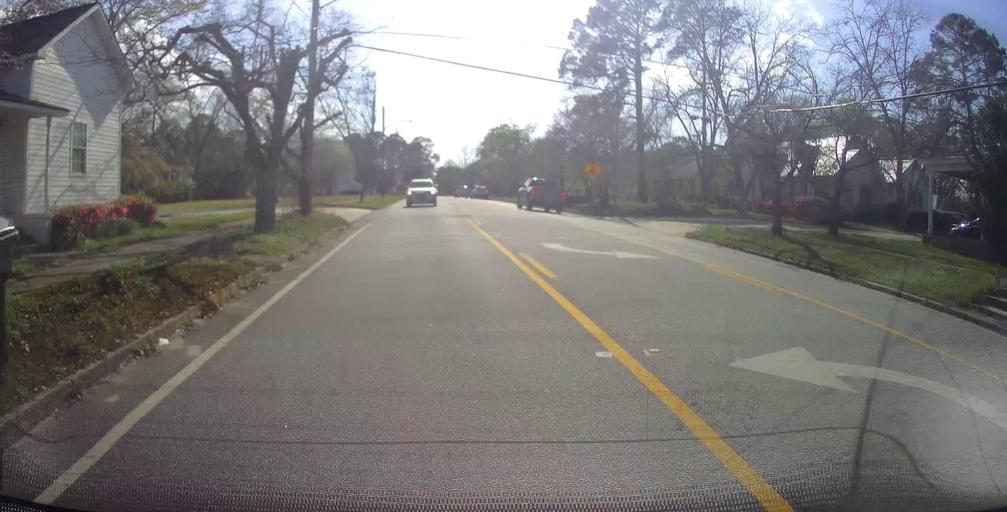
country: US
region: Georgia
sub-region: Dodge County
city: Eastman
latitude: 32.1949
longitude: -83.1817
